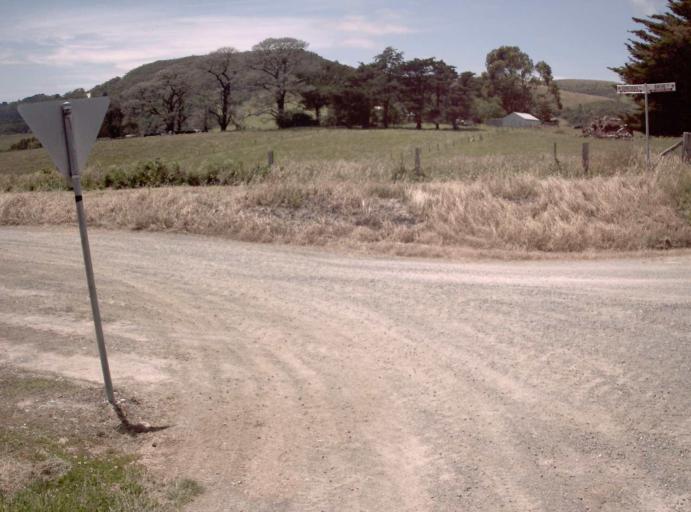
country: AU
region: Victoria
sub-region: Bass Coast
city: North Wonthaggi
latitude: -38.7152
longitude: 146.1005
